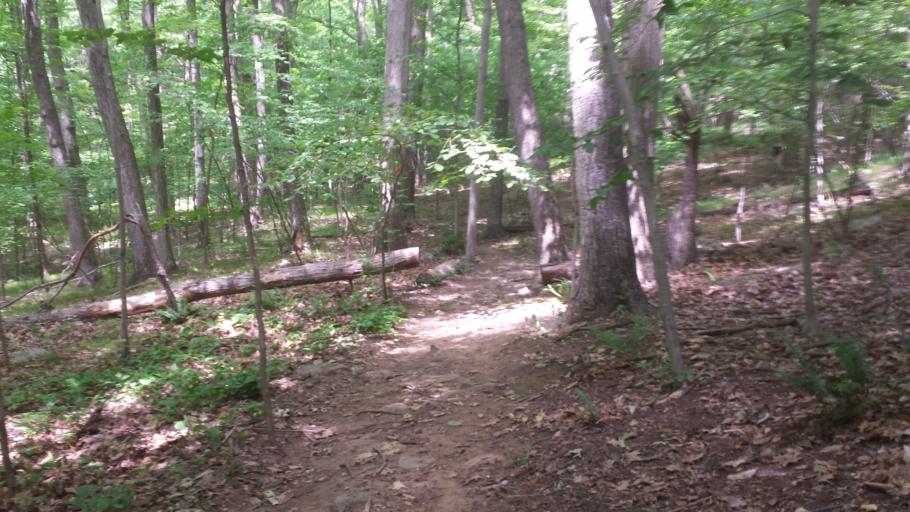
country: US
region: New York
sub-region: Putnam County
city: Peach Lake
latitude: 41.3066
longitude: -73.5700
